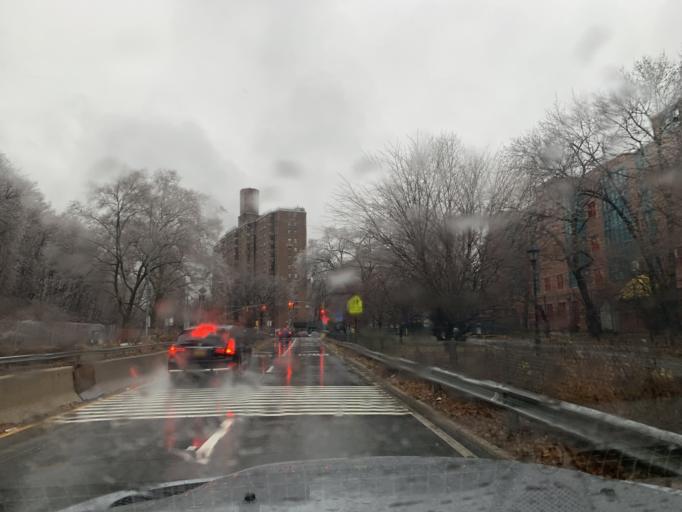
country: US
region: New York
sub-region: New York County
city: Inwood
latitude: 40.8581
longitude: -73.9228
